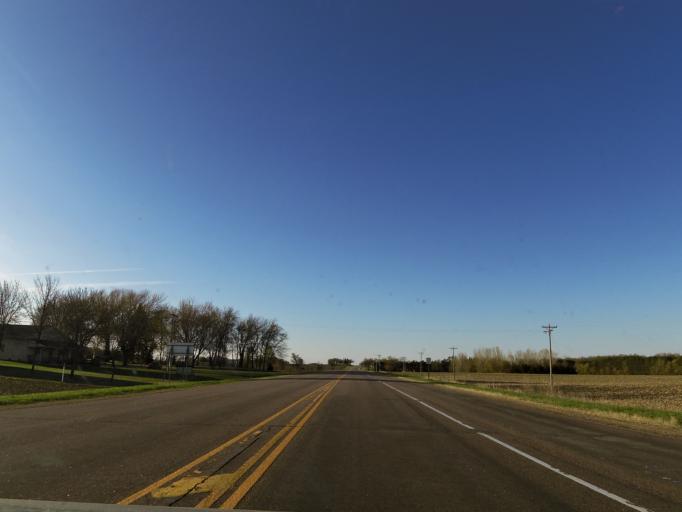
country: US
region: Wisconsin
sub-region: Pierce County
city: Prescott
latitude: 44.6047
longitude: -92.7724
